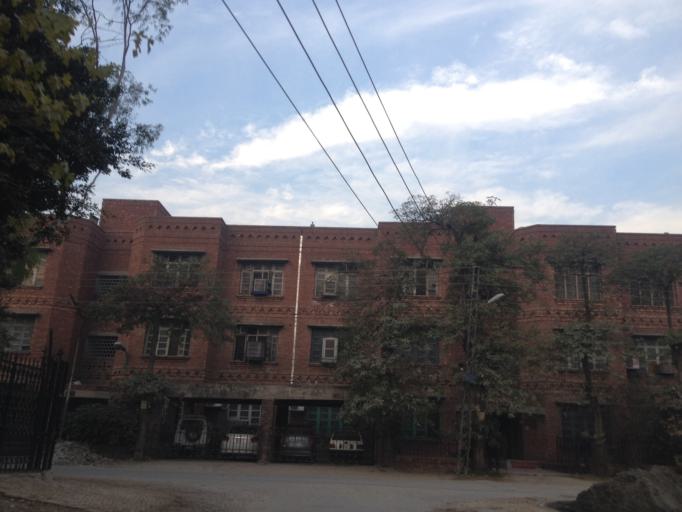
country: PK
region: Punjab
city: Lahore
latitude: 31.4645
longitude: 74.3003
